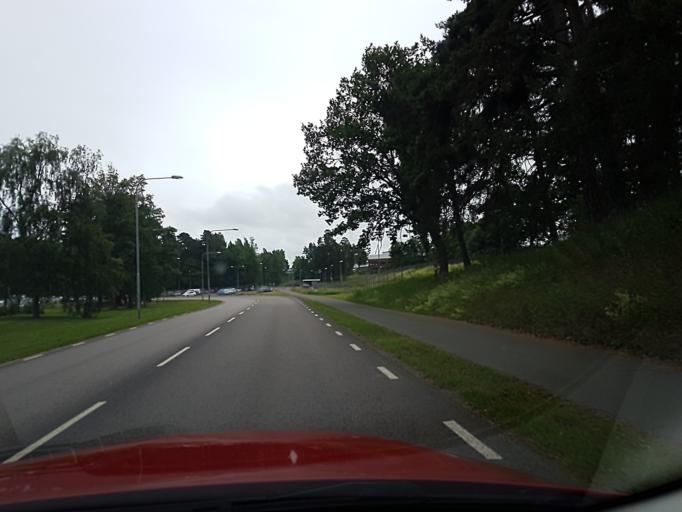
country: SE
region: Vaestra Goetaland
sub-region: Skovde Kommun
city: Skoevde
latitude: 58.3841
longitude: 13.8606
